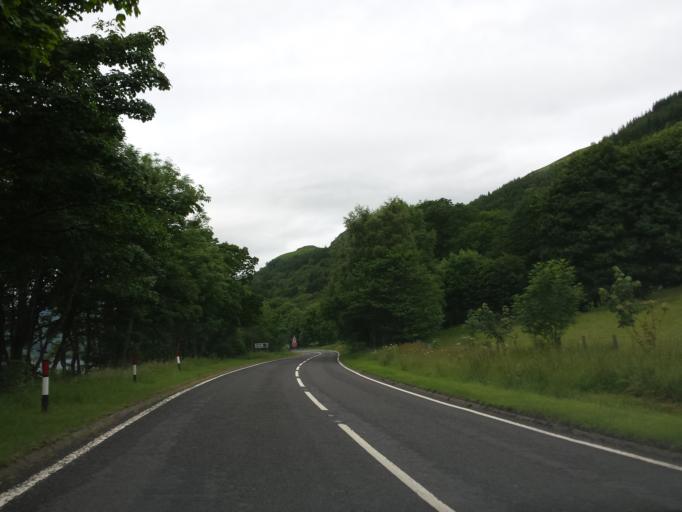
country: GB
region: Scotland
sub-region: Stirling
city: Callander
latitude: 56.3907
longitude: -4.2034
